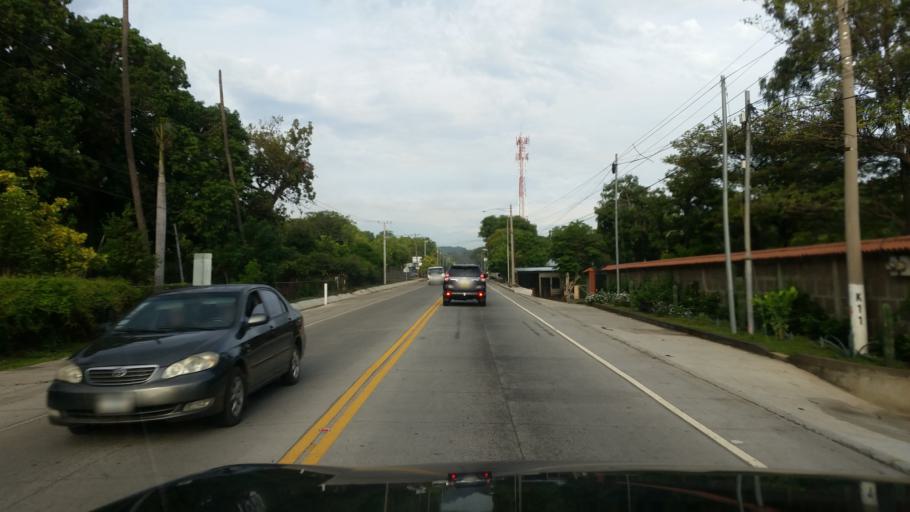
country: NI
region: Managua
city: Ciudad Sandino
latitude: 12.1024
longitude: -86.3373
